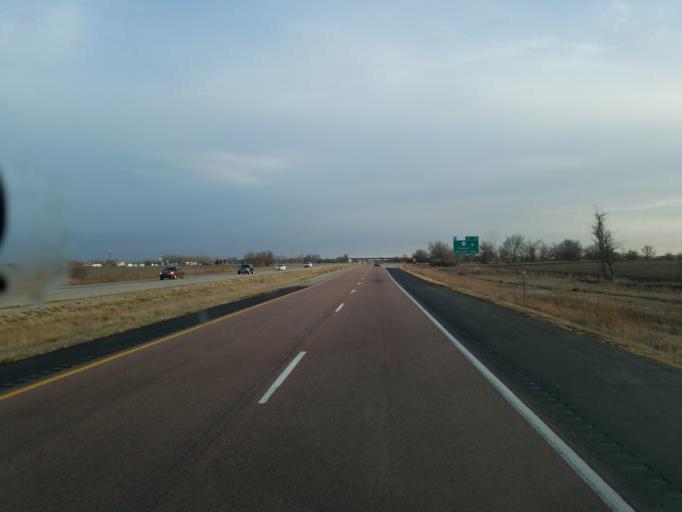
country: US
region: Iowa
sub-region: Monona County
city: Onawa
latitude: 42.0326
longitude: -96.1373
